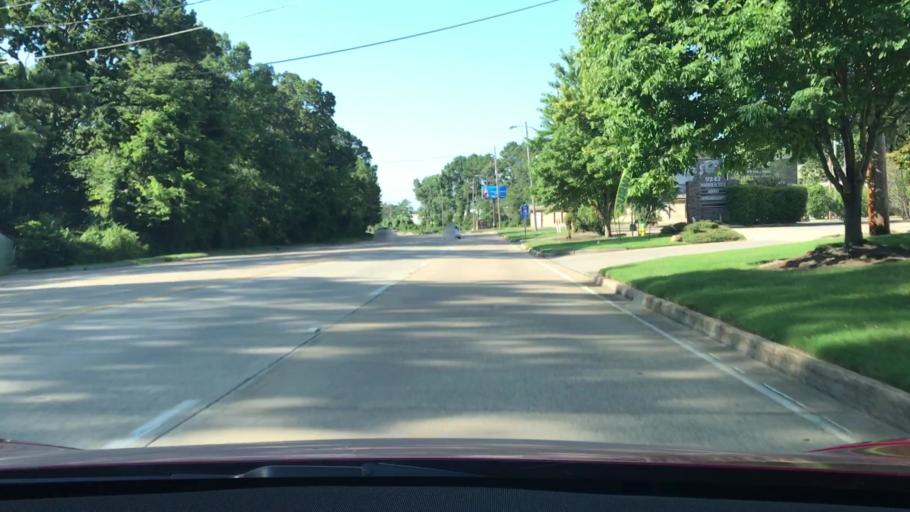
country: US
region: Louisiana
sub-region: Bossier Parish
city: Bossier City
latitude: 32.4083
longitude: -93.7386
